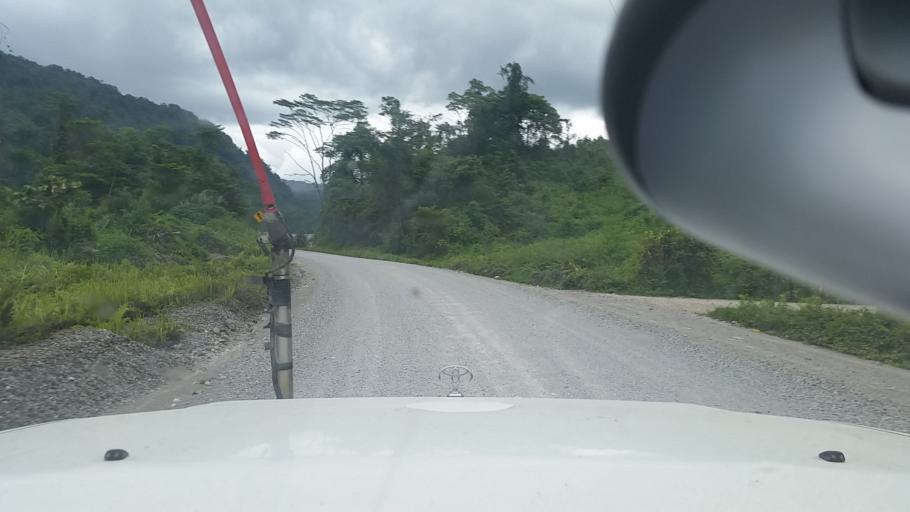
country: ID
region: Papua
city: Mindiptana
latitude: -5.3081
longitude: 141.2523
